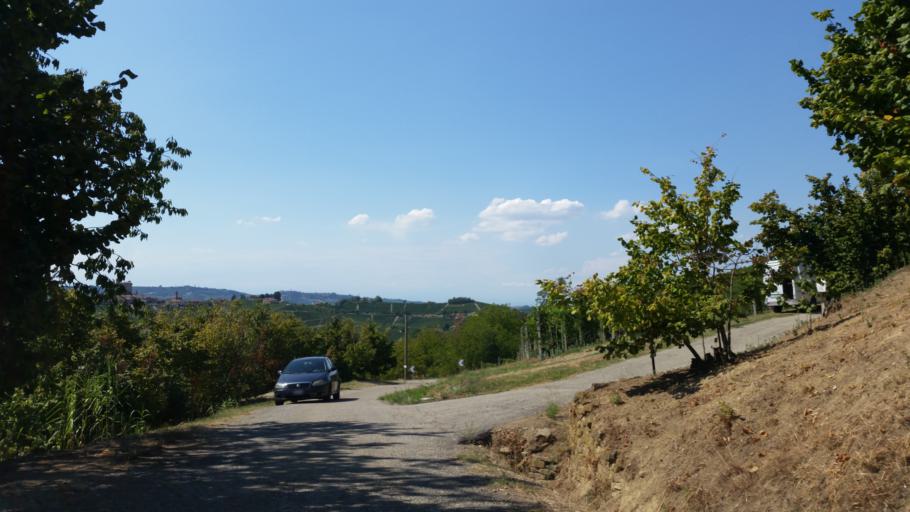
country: IT
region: Piedmont
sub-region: Provincia di Cuneo
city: Sinio
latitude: 44.6067
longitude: 8.0213
